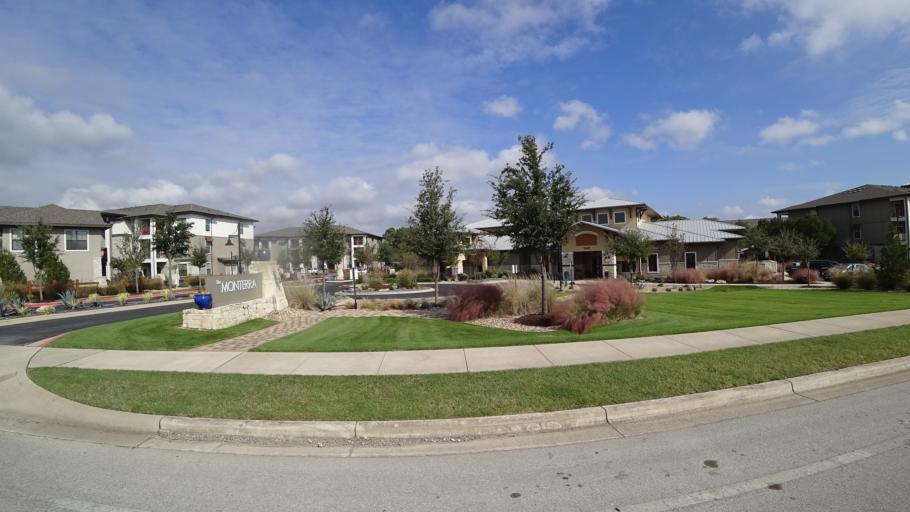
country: US
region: Texas
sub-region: Williamson County
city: Jollyville
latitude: 30.4382
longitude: -97.7337
